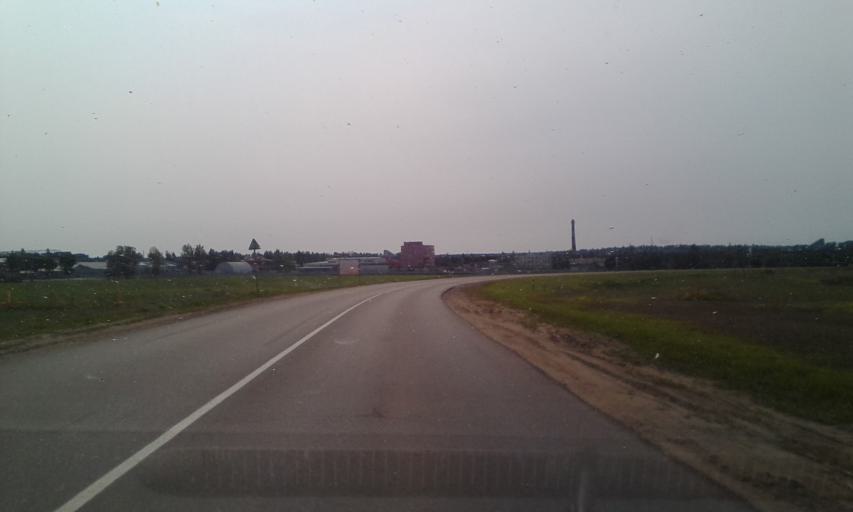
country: BY
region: Minsk
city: Hatava
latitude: 53.7827
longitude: 27.6543
